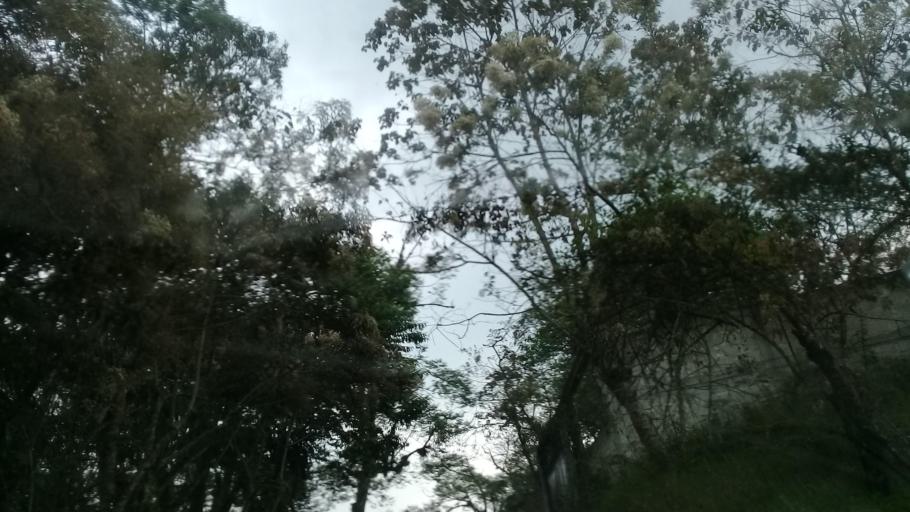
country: MX
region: Veracruz
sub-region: Xalapa
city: Fraccionamiento las Fuentes
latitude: 19.4928
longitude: -96.8969
